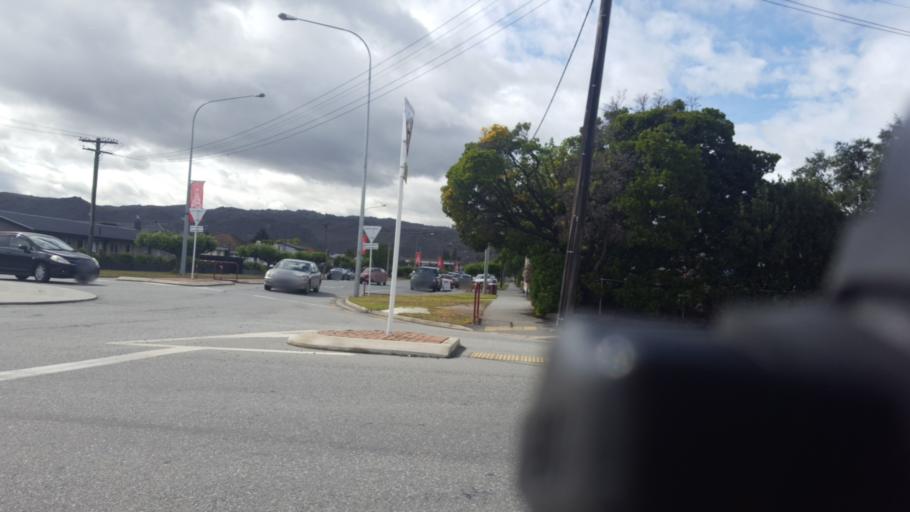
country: NZ
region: Otago
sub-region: Queenstown-Lakes District
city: Wanaka
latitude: -45.2478
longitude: 169.3840
